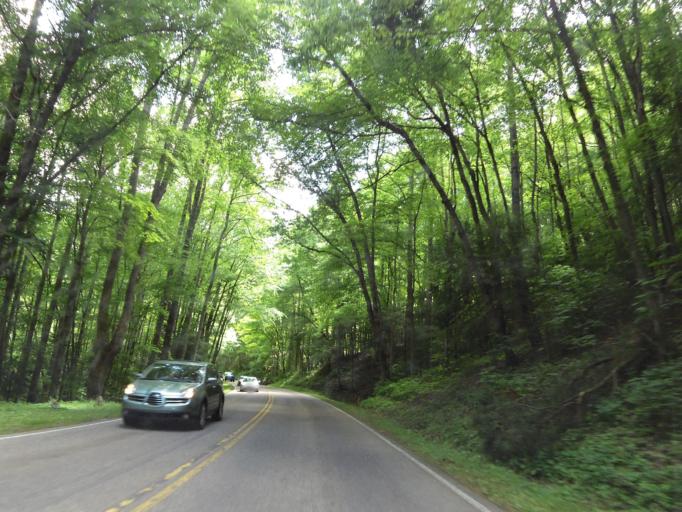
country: US
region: Tennessee
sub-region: Sevier County
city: Gatlinburg
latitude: 35.6687
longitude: -83.5276
